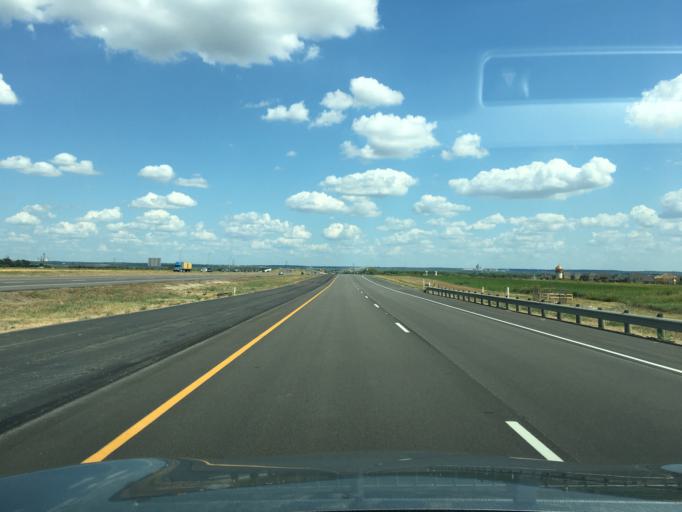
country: US
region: Texas
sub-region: Tarrant County
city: Mansfield
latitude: 32.5273
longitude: -97.0922
